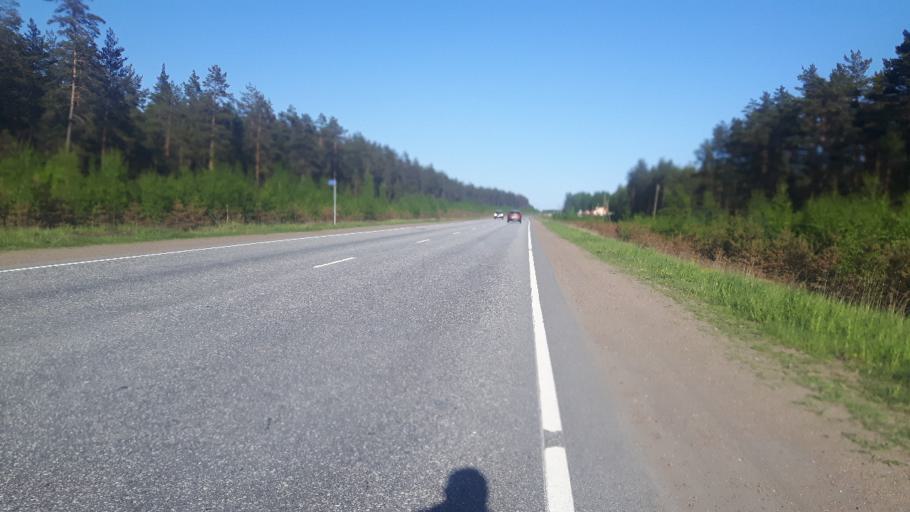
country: RU
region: Leningrad
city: Sosnovyy Bor
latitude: 60.1695
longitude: 29.1977
